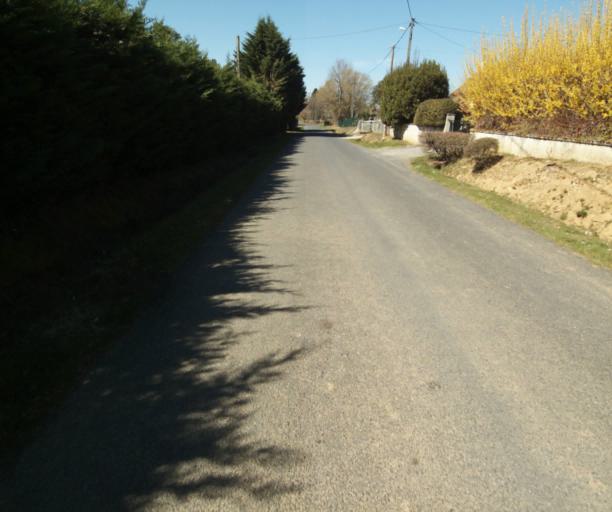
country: FR
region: Limousin
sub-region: Departement de la Correze
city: Chamboulive
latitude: 45.4383
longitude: 1.6892
